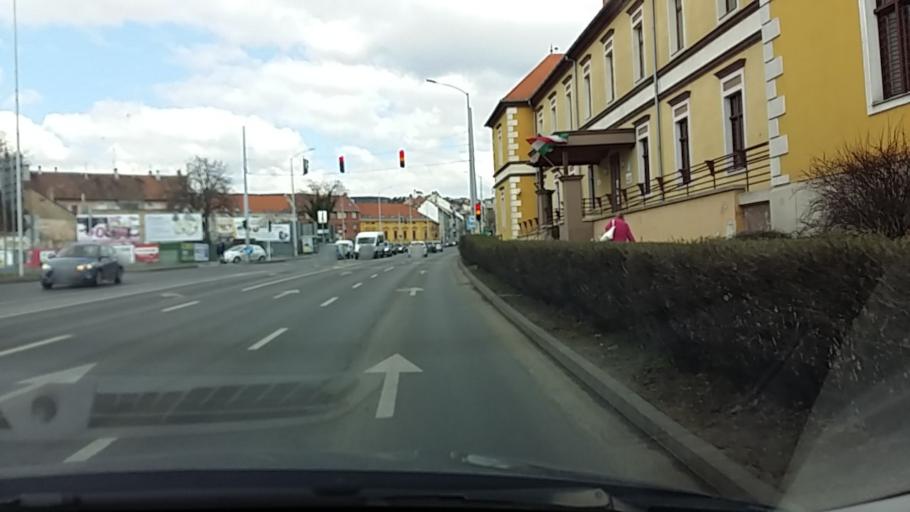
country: HU
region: Baranya
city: Pecs
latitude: 46.0726
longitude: 18.2336
